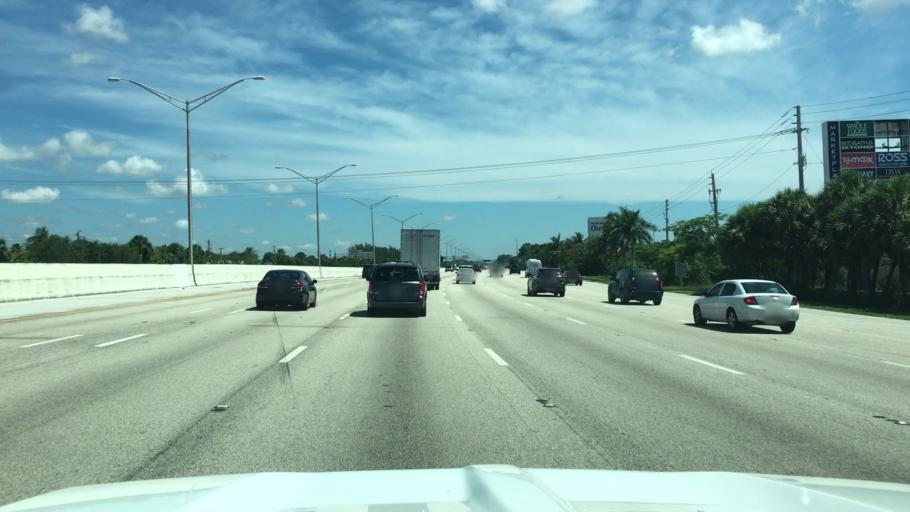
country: US
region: Florida
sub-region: Palm Beach County
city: Schall Circle
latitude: 26.7176
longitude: -80.0865
